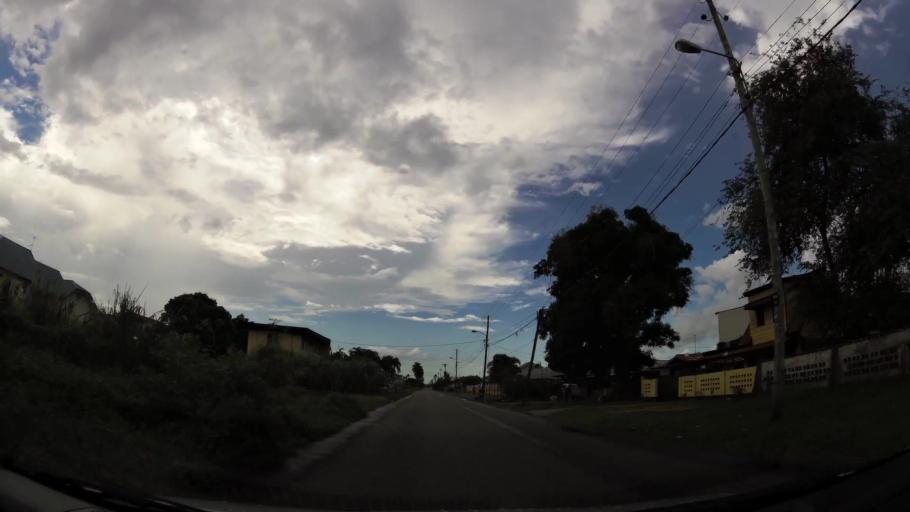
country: SR
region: Paramaribo
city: Paramaribo
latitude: 5.8415
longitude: -55.1221
